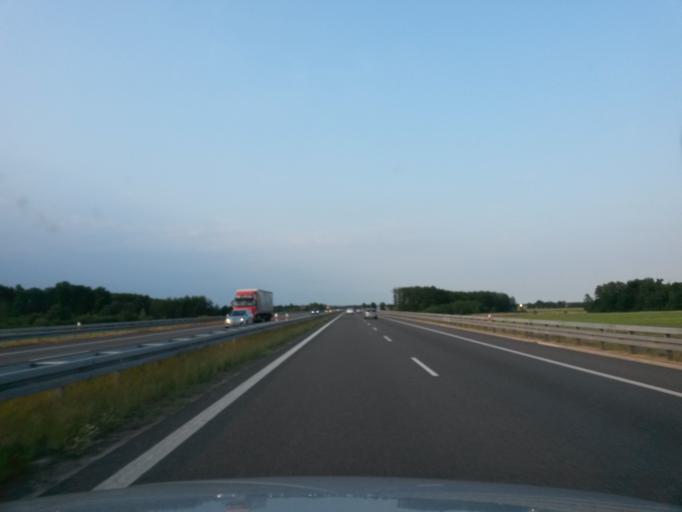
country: PL
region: Lower Silesian Voivodeship
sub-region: Powiat olesnicki
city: Olesnica
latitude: 51.2441
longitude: 17.5092
